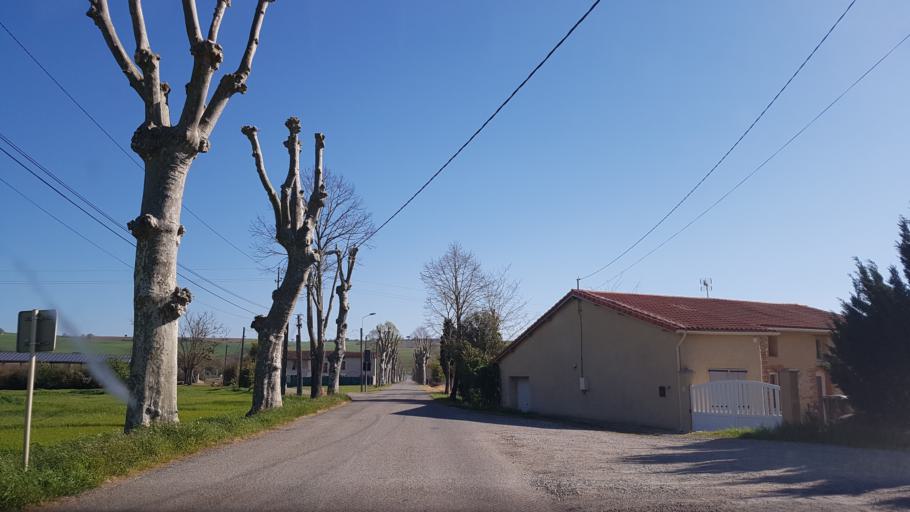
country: FR
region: Midi-Pyrenees
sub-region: Departement de l'Ariege
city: Mazeres
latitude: 43.2558
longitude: 1.6836
